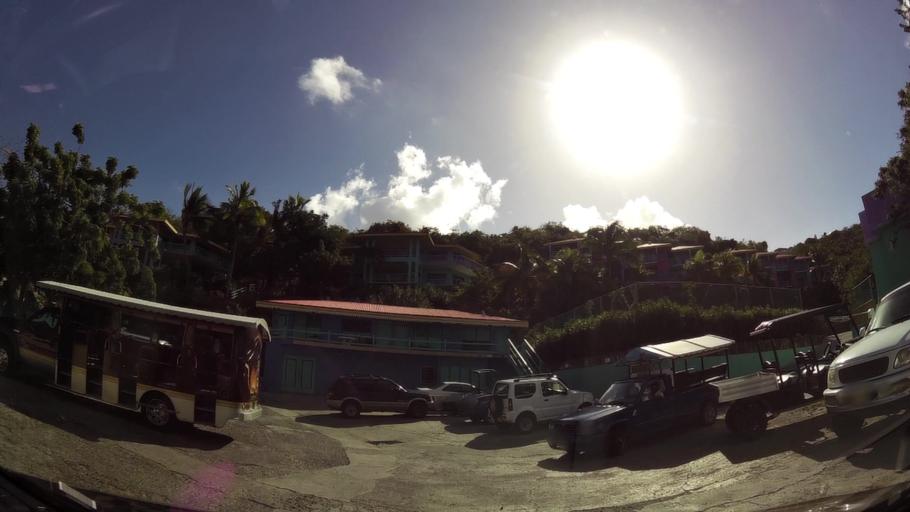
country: VG
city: Tortola
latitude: 18.4970
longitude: -64.3859
